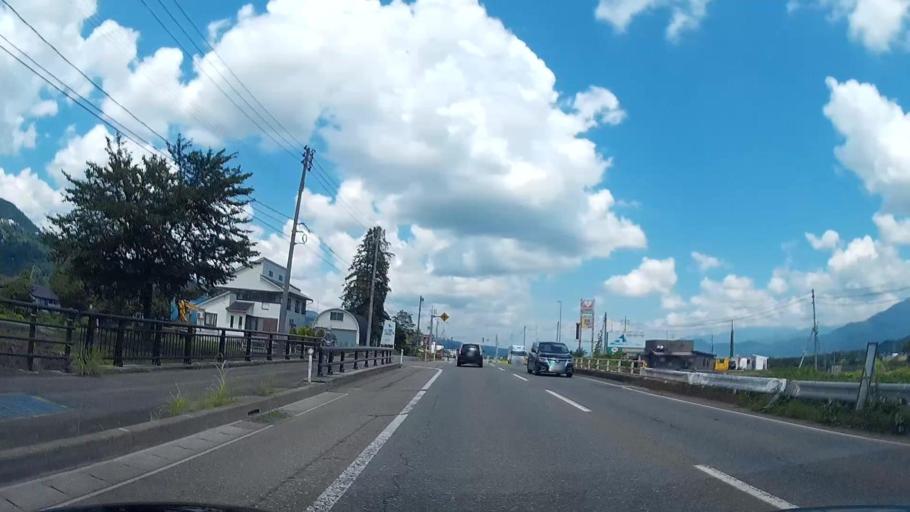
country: JP
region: Niigata
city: Shiozawa
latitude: 36.9942
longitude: 138.8121
